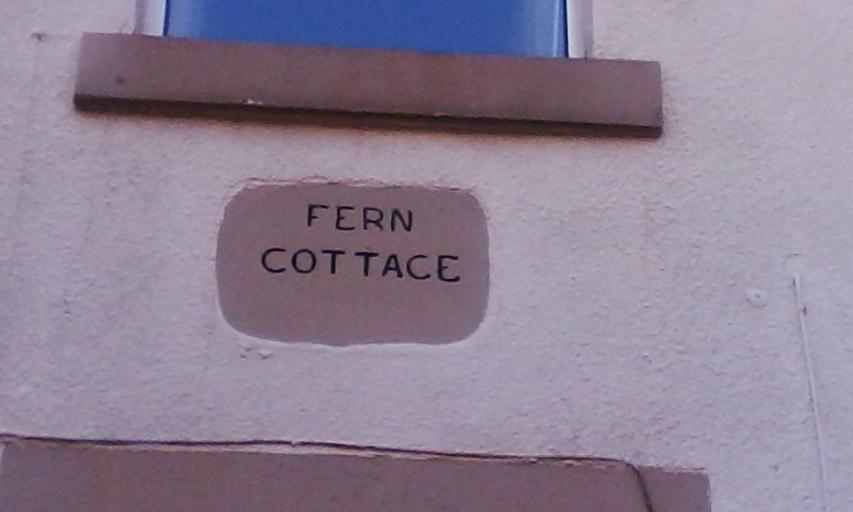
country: GB
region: England
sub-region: Nottinghamshire
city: Arnold
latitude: 52.9754
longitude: -1.1205
